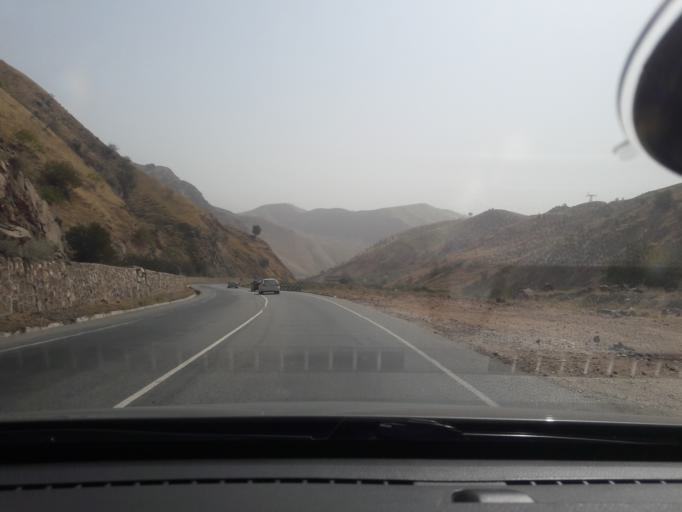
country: TJ
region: Khatlon
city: Norak
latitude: 38.4304
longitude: 69.2241
